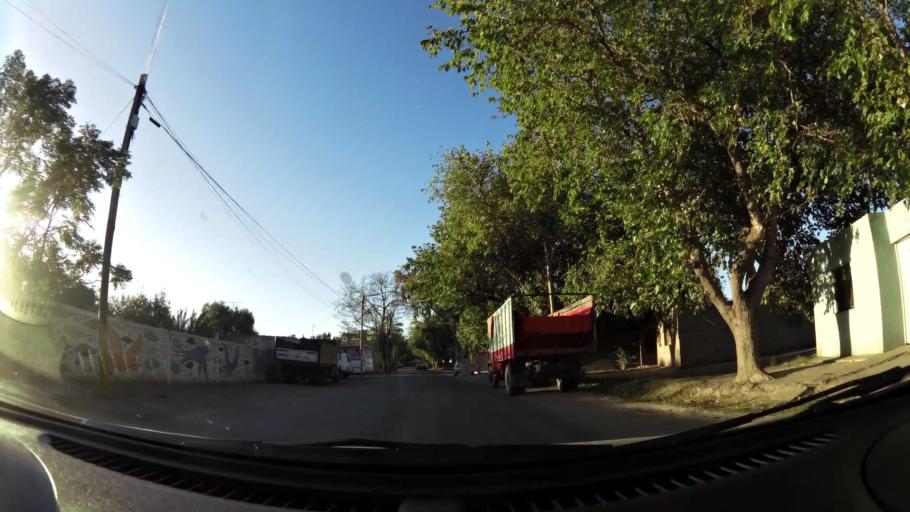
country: AR
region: San Juan
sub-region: Departamento de Santa Lucia
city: Santa Lucia
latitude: -31.5530
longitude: -68.4759
